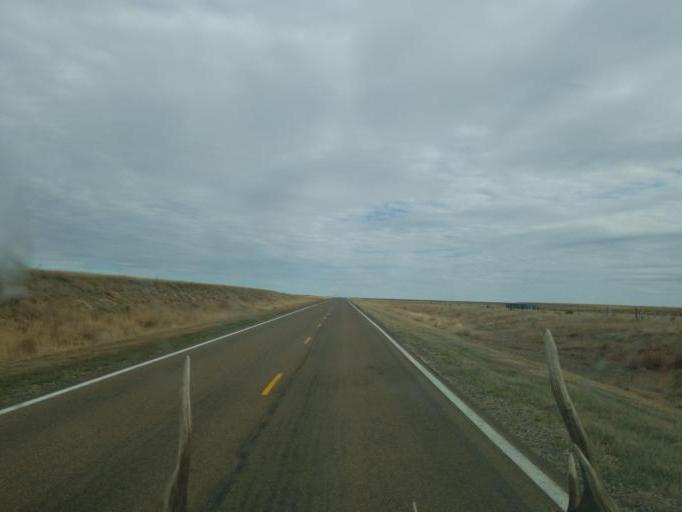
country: US
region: Kansas
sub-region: Thomas County
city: Colby
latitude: 39.0289
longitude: -101.3033
